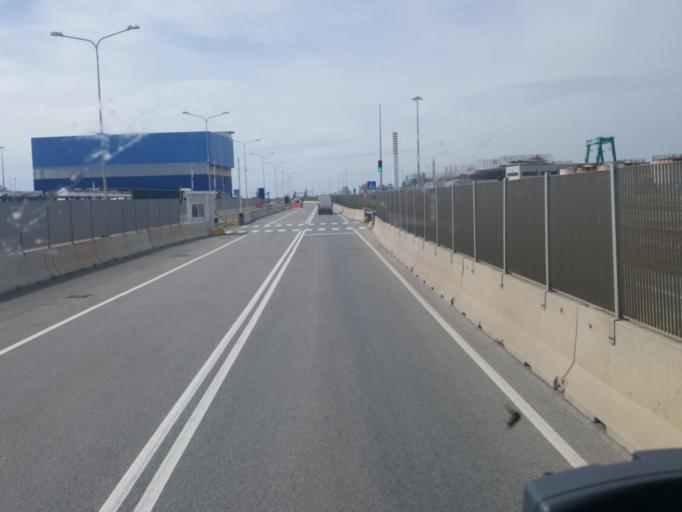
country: IT
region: Latium
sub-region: Citta metropolitana di Roma Capitale
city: Civitavecchia
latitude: 42.1066
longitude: 11.7776
